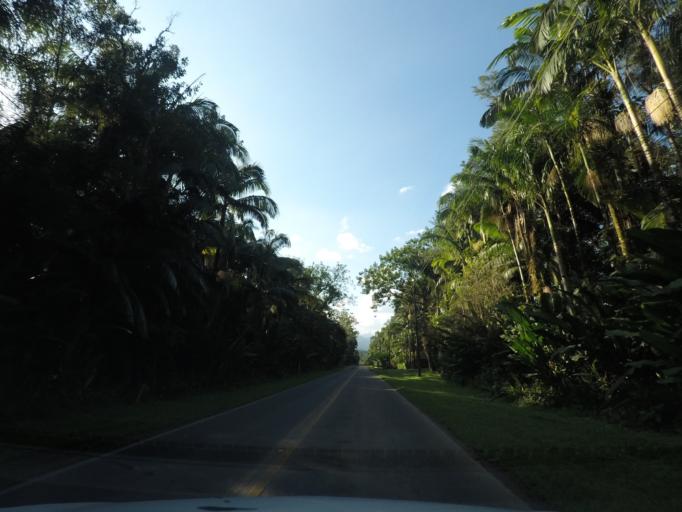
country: BR
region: Parana
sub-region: Antonina
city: Antonina
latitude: -25.4166
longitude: -48.8738
